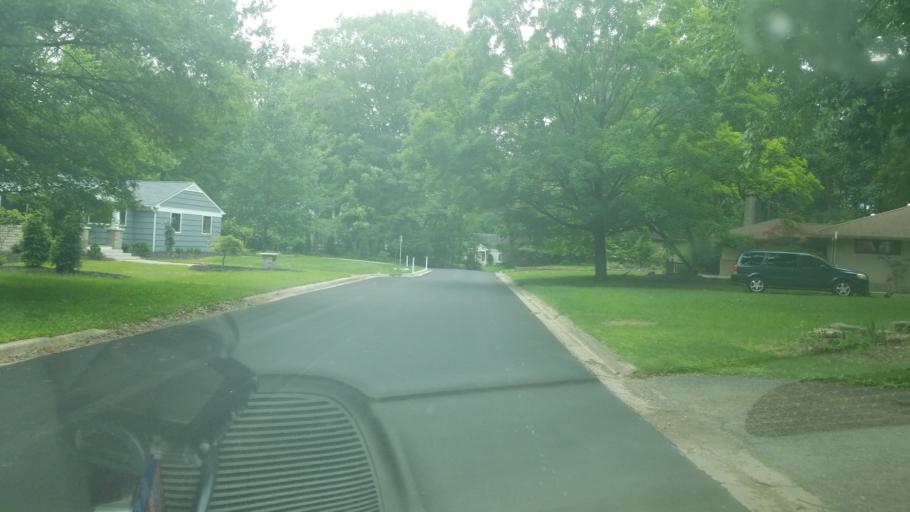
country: US
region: Ohio
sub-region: Franklin County
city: Worthington
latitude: 40.0453
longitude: -83.0036
